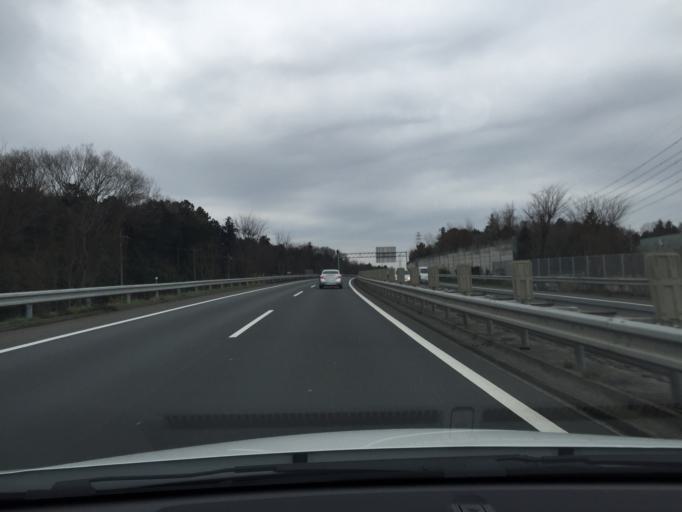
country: JP
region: Saitama
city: Sayama
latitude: 35.9017
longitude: 139.3902
